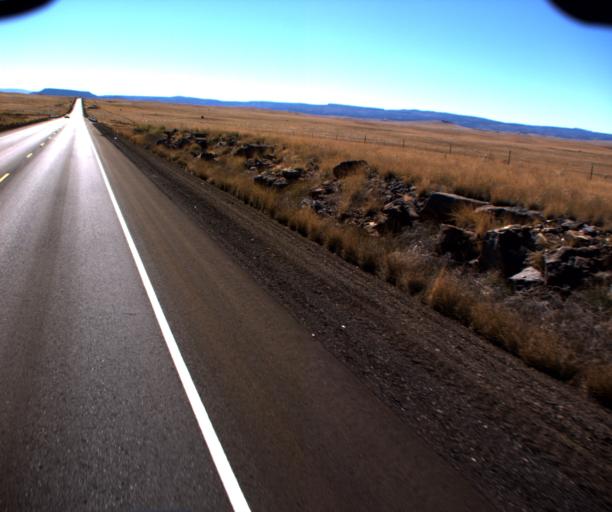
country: US
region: Arizona
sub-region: Apache County
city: Springerville
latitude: 34.2181
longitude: -109.3343
